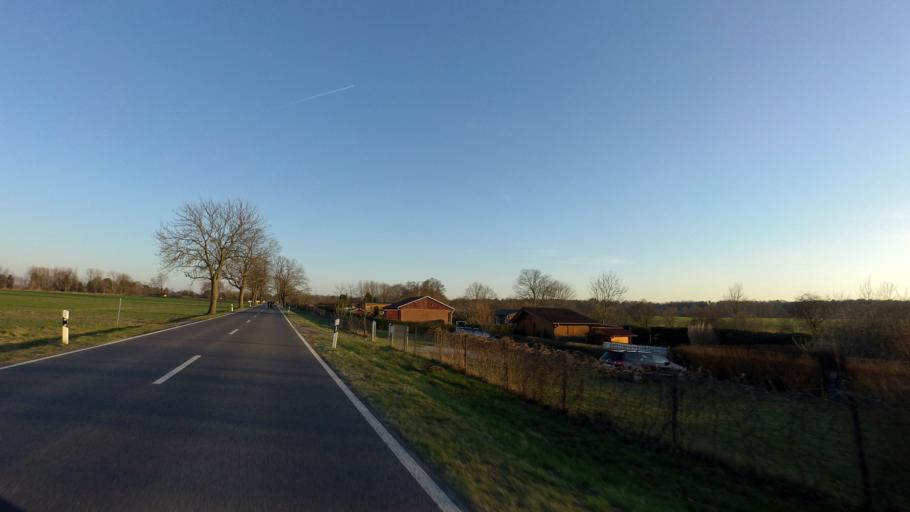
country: DE
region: Berlin
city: Hellersdorf
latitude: 52.5666
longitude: 13.6257
